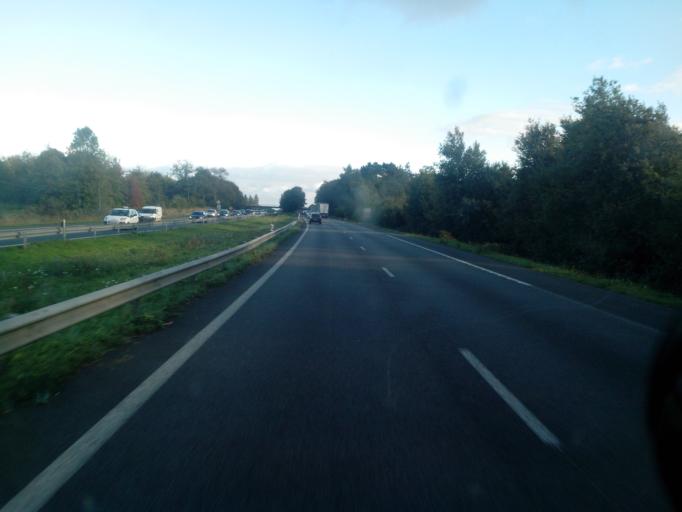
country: FR
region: Pays de la Loire
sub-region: Departement de la Loire-Atlantique
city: Vigneux-de-Bretagne
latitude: 47.3034
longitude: -1.7583
